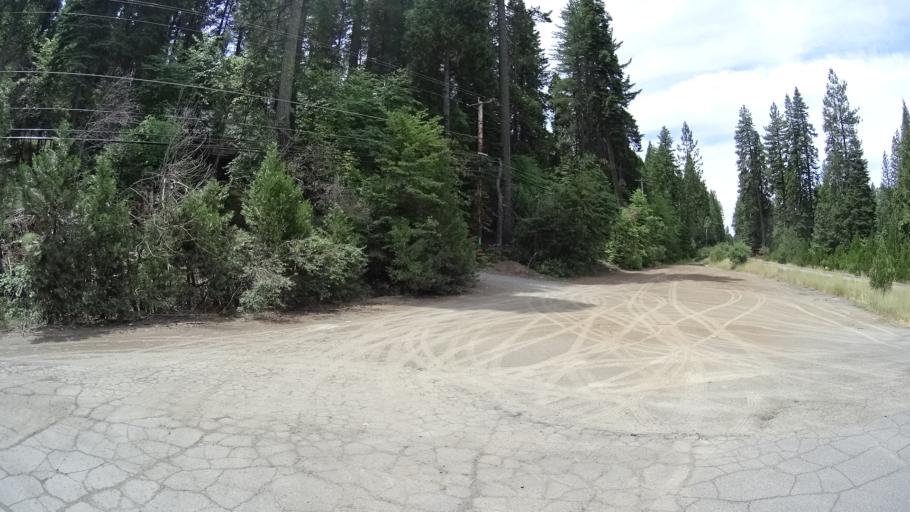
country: US
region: California
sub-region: Calaveras County
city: Arnold
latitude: 38.2576
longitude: -120.3426
